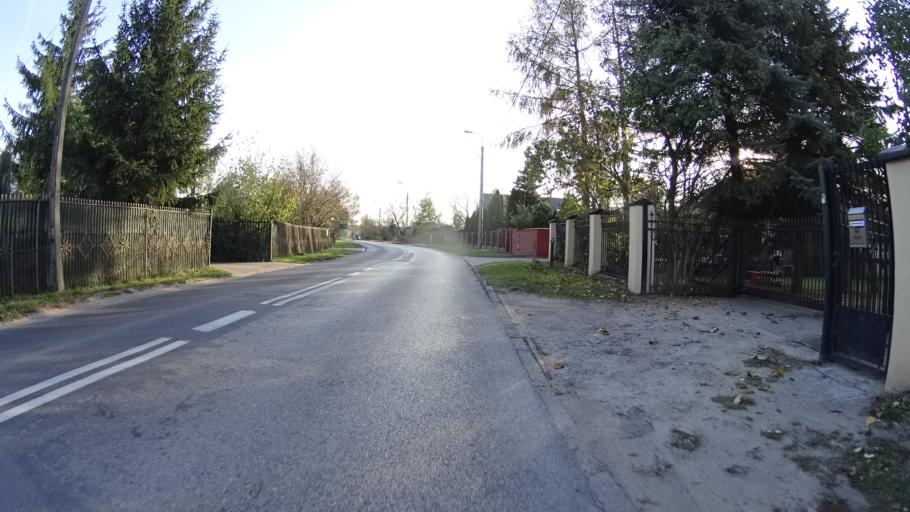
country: PL
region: Masovian Voivodeship
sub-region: Powiat warszawski zachodni
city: Babice
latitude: 52.2865
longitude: 20.8670
